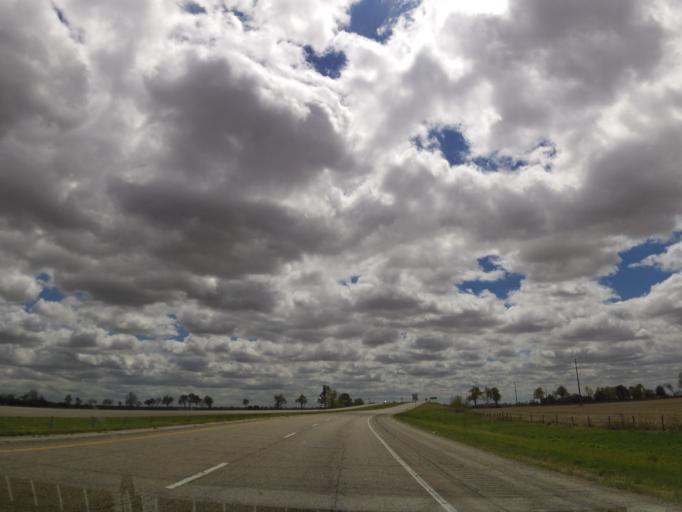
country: US
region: Arkansas
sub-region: Poinsett County
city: Trumann
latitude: 35.6252
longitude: -90.4969
